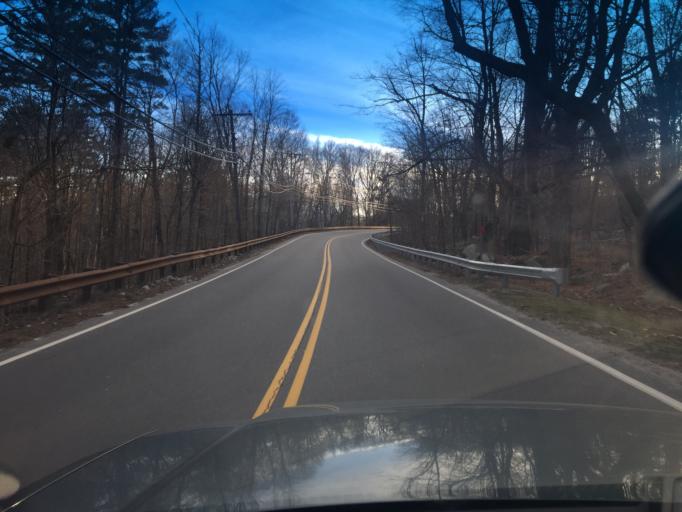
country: US
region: Massachusetts
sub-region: Middlesex County
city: Sherborn
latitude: 42.2342
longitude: -71.3808
